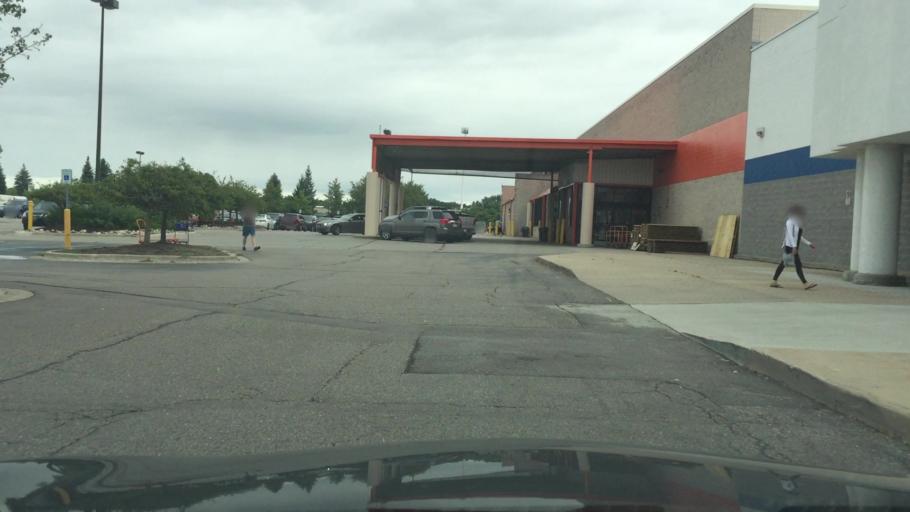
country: US
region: Michigan
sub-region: Oakland County
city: Walled Lake
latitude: 42.5327
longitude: -83.4412
